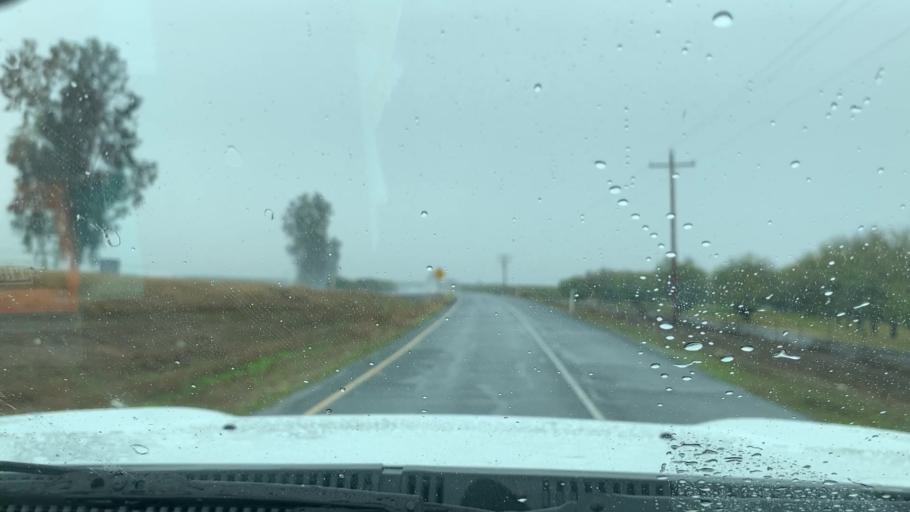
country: US
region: California
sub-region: Tulare County
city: Earlimart
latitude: 35.8359
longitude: -119.2606
